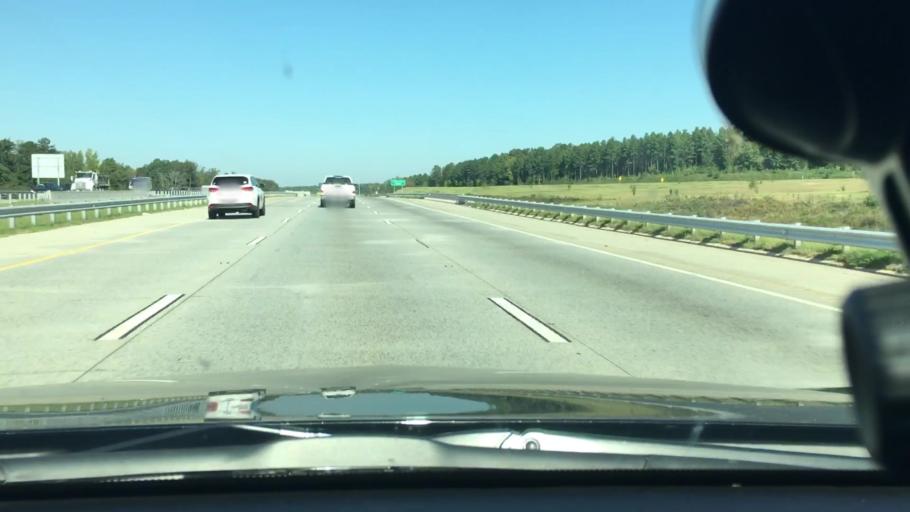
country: US
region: North Carolina
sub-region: Cabarrus County
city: Harrisburg
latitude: 35.3494
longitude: -80.7341
